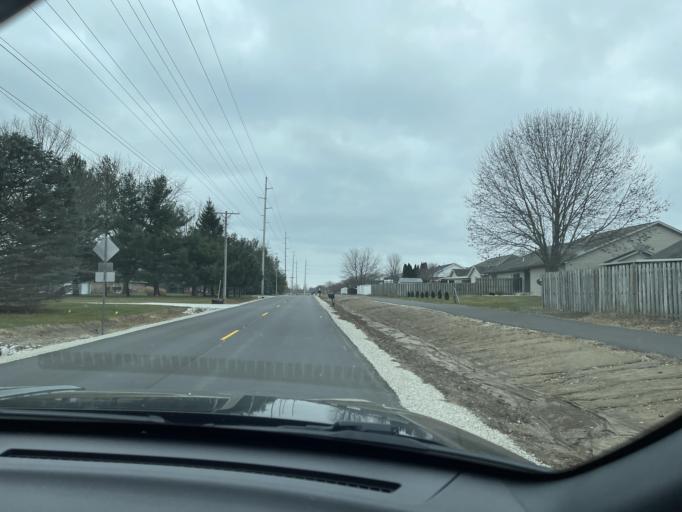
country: US
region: Illinois
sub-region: Sangamon County
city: Rochester
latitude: 39.7584
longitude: -89.5787
